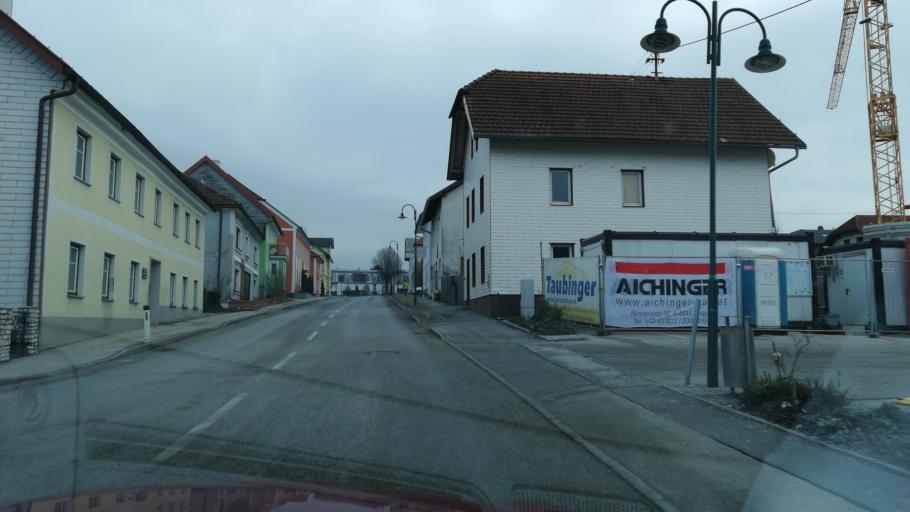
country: AT
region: Upper Austria
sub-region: Politischer Bezirk Vocklabruck
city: Niederthalheim
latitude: 48.1866
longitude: 13.7419
